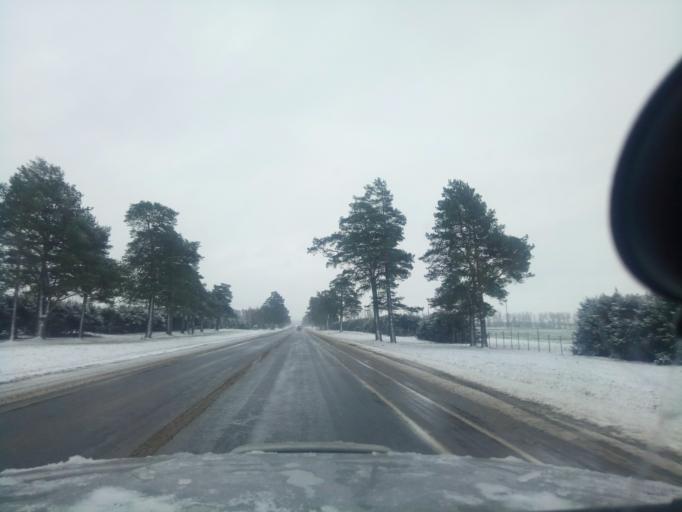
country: BY
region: Minsk
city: Nyasvizh
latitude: 53.2513
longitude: 26.6204
